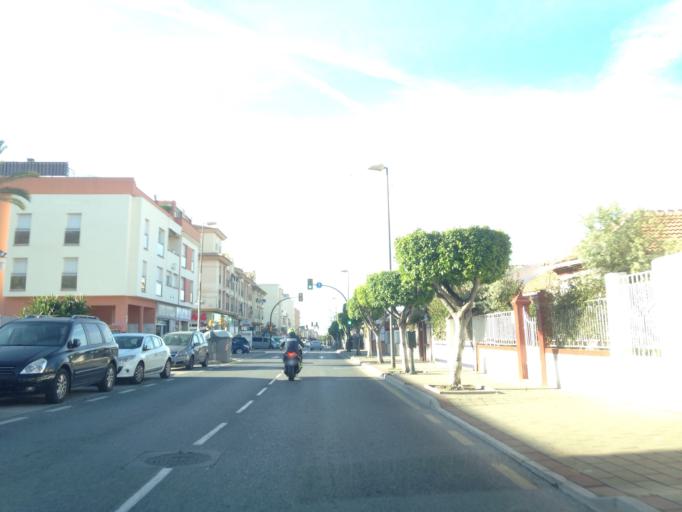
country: ES
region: Andalusia
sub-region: Provincia de Malaga
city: Malaga
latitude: 36.7482
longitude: -4.4217
